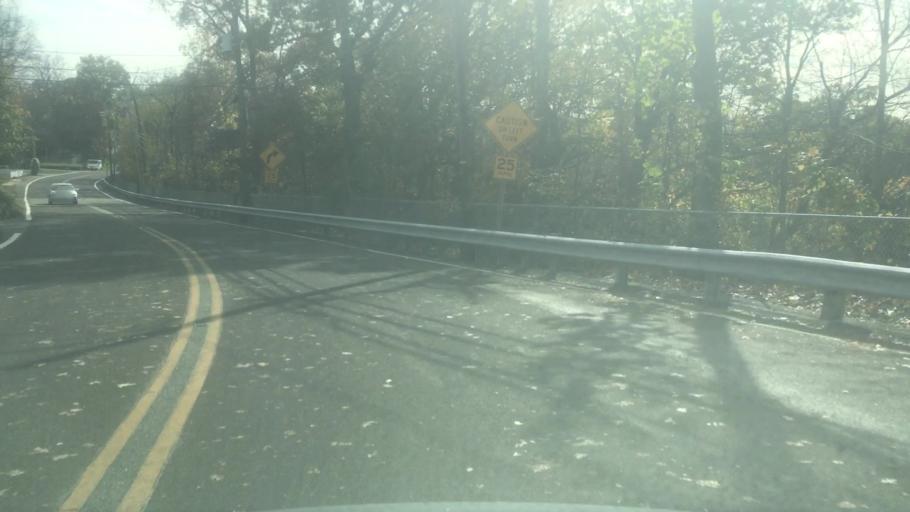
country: US
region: New Jersey
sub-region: Morris County
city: Butler
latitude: 41.0077
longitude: -74.3350
